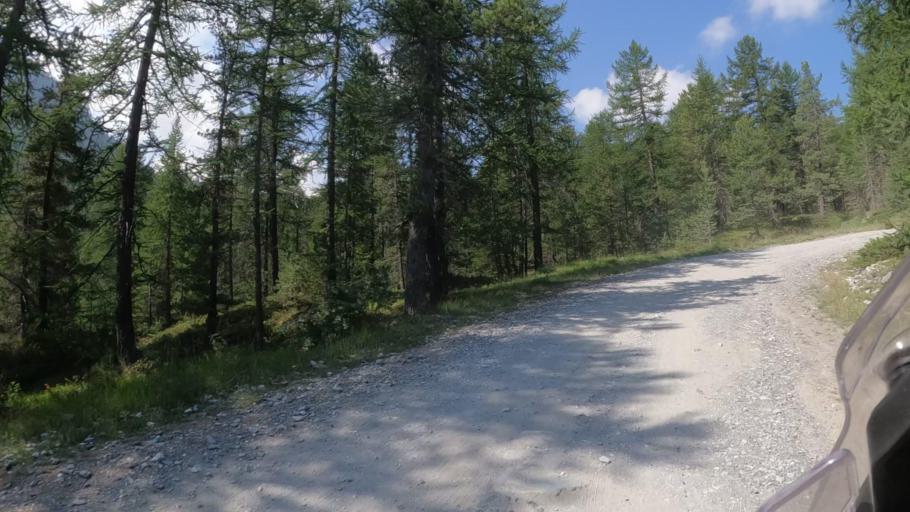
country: IT
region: Piedmont
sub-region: Provincia di Torino
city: Cesana Torinese
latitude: 44.9158
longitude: 6.8033
